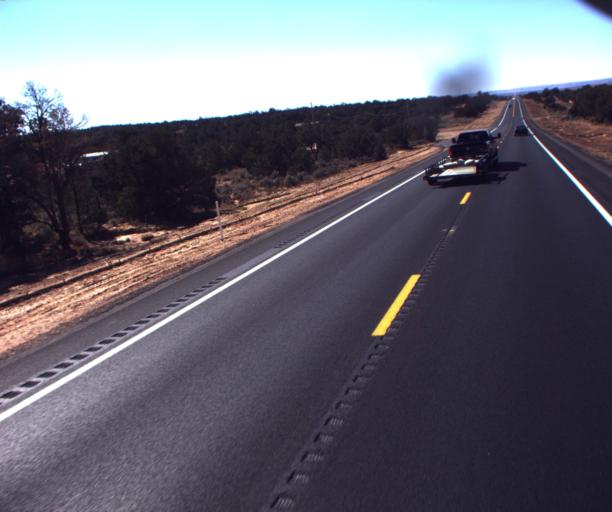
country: US
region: Arizona
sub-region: Apache County
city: Ganado
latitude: 35.7189
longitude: -109.3816
